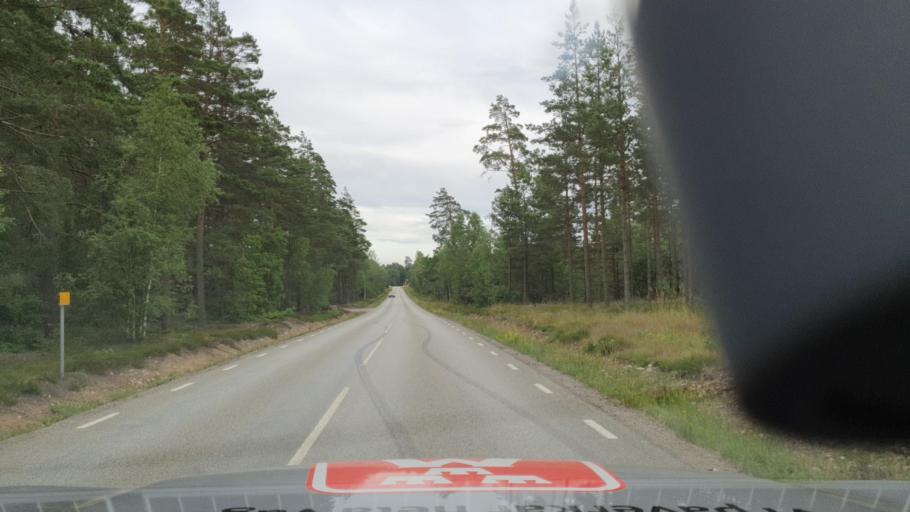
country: SE
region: Kalmar
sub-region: Kalmar Kommun
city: Trekanten
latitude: 56.6413
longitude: 16.0236
